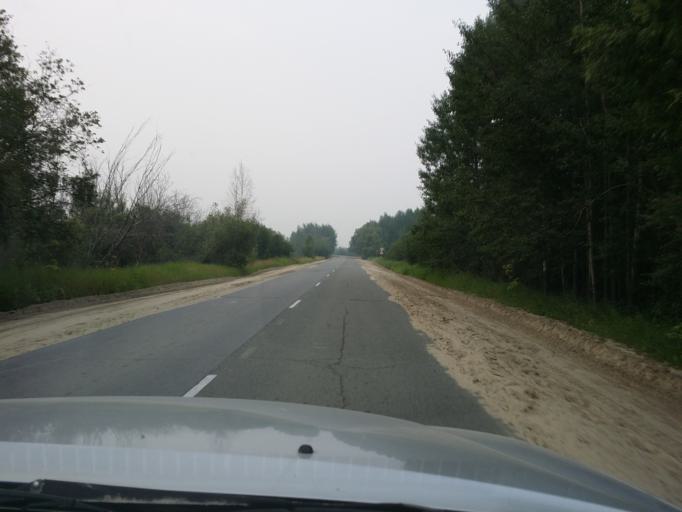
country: RU
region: Khanty-Mansiyskiy Avtonomnyy Okrug
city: Megion
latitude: 61.0114
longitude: 76.3130
